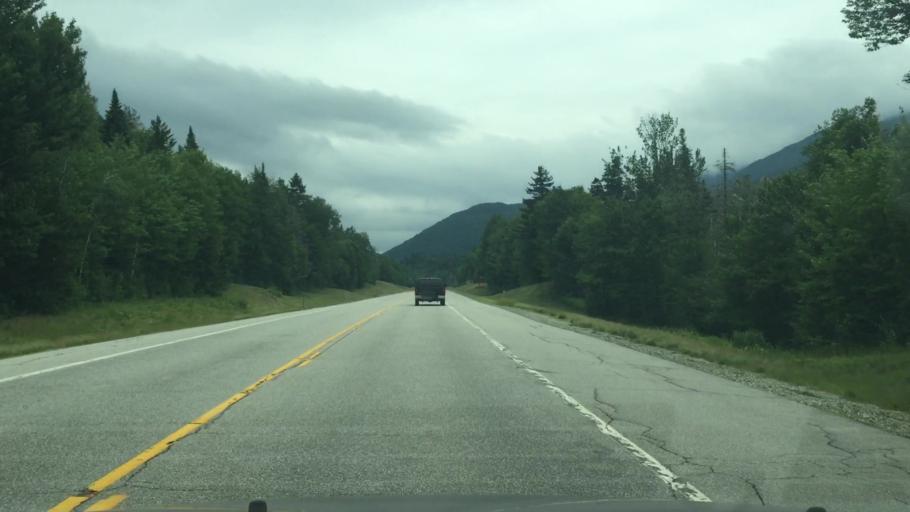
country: US
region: New Hampshire
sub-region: Coos County
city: Jefferson
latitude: 44.2361
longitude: -71.4228
